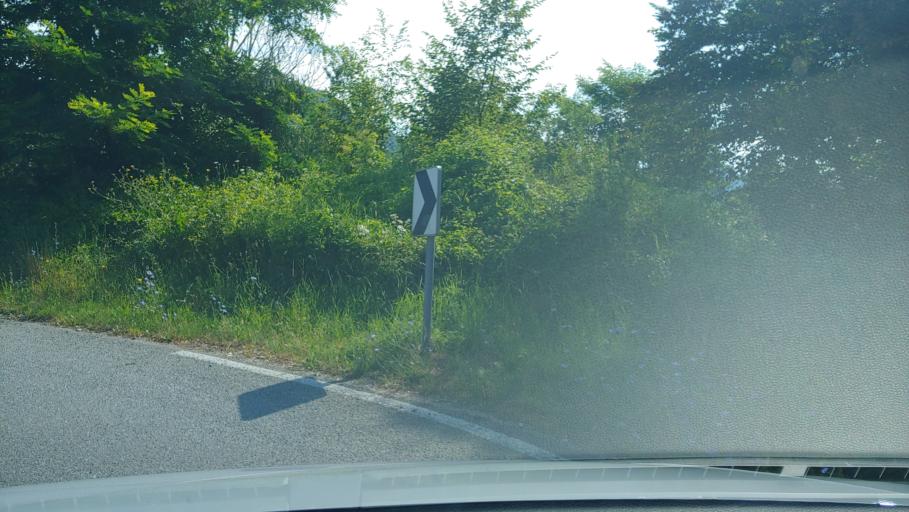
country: SI
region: Komen
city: Komen
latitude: 45.8525
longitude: 13.7951
